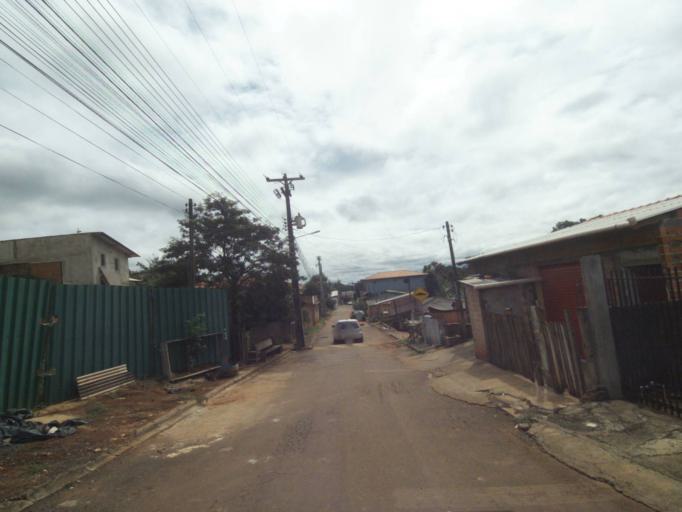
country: BR
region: Parana
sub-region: Telemaco Borba
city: Telemaco Borba
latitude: -24.3302
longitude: -50.6363
